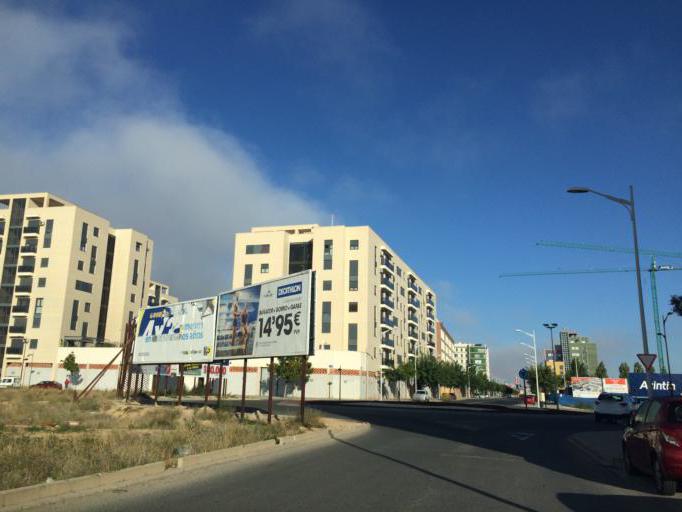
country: ES
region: Castille-La Mancha
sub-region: Provincia de Albacete
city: Albacete
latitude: 39.0045
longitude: -1.8717
